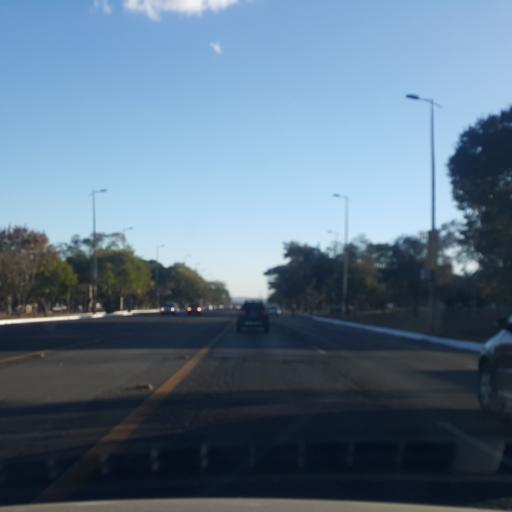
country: BR
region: Federal District
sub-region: Brasilia
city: Brasilia
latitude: -15.8312
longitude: -47.9204
